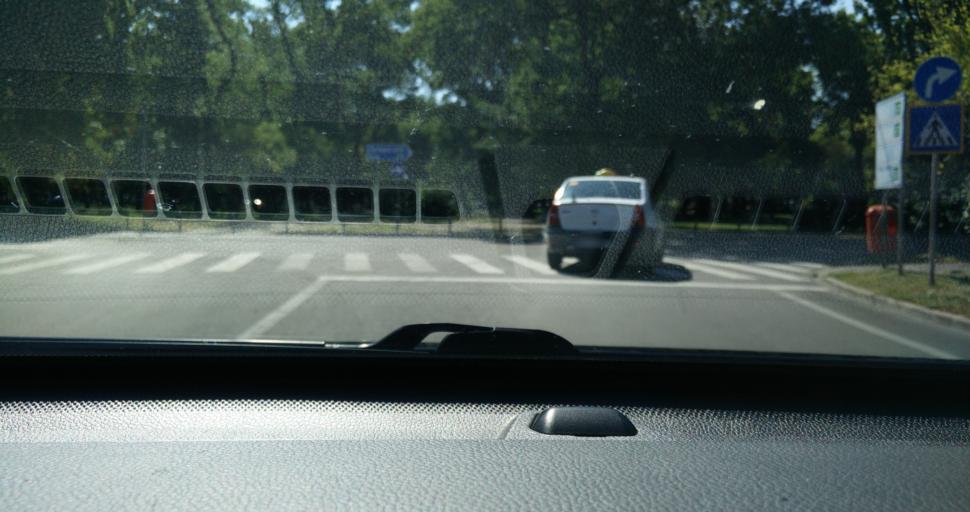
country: RO
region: Bihor
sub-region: Comuna Biharea
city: Oradea
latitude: 47.0444
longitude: 21.9338
